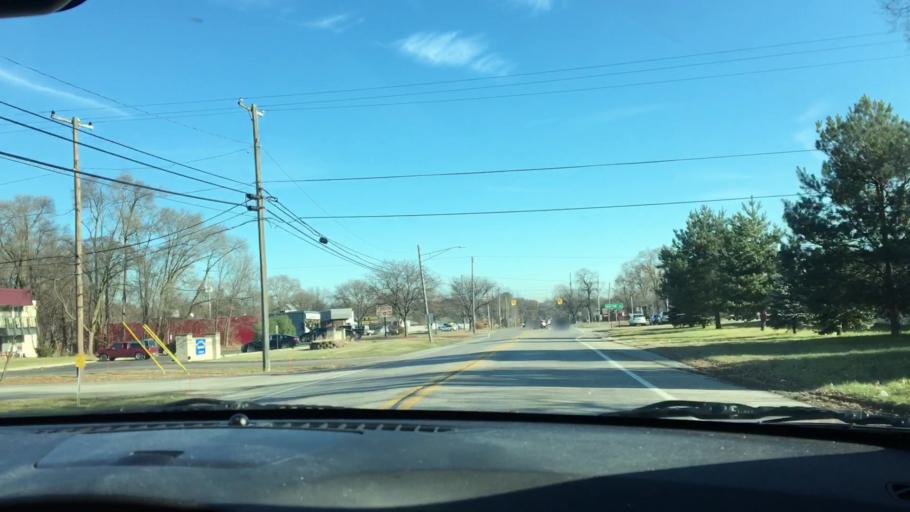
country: US
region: Michigan
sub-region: Wayne County
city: Westland
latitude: 42.3561
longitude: -83.3888
